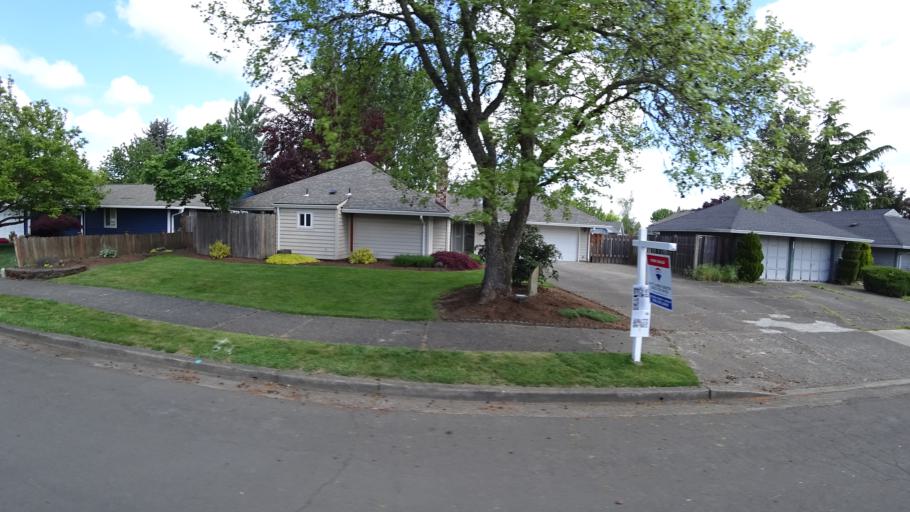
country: US
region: Oregon
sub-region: Washington County
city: Aloha
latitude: 45.5024
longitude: -122.8825
